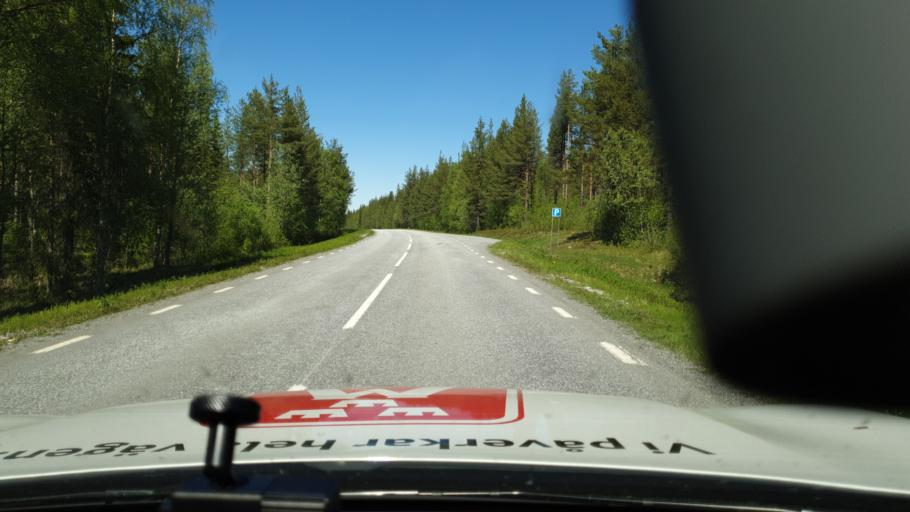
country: SE
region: Vaesterbotten
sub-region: Storumans Kommun
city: Storuman
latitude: 65.1157
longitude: 17.1203
